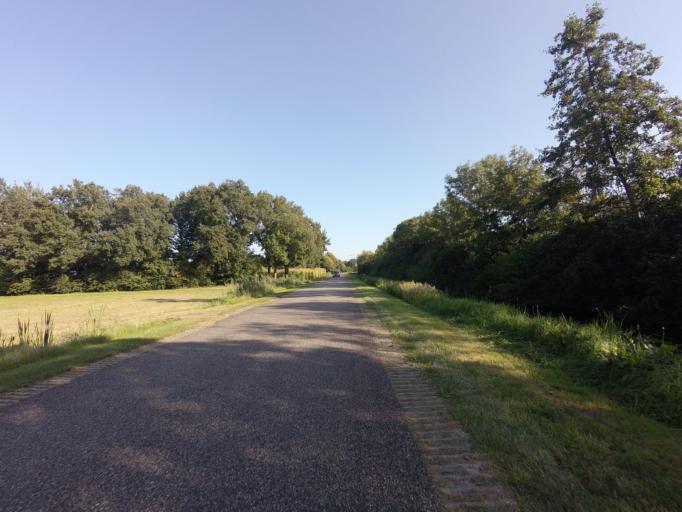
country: NL
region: Overijssel
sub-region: Gemeente Hardenberg
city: Hardenberg
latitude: 52.5543
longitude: 6.6497
